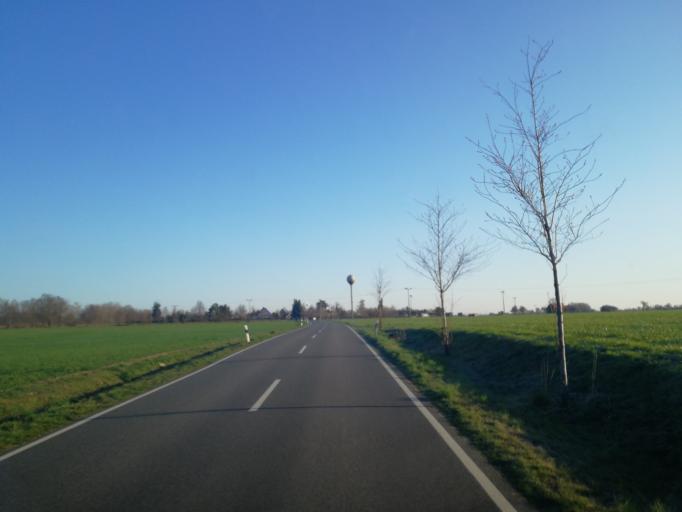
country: DE
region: Brandenburg
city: Luckau
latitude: 51.8260
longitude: 13.6423
